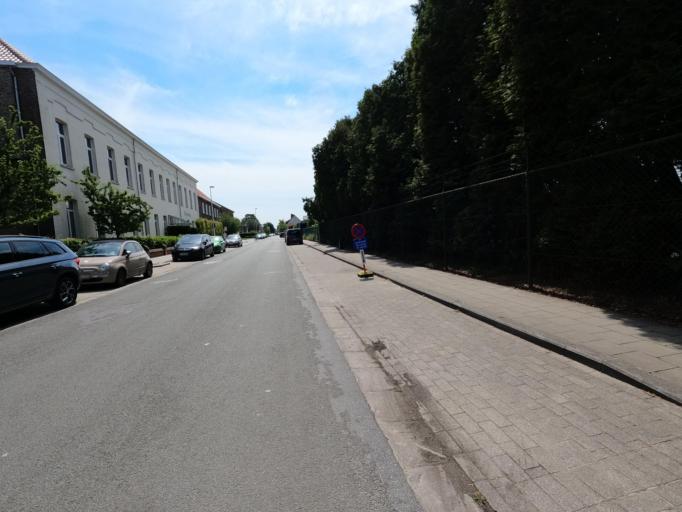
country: BE
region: Flanders
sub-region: Provincie Antwerpen
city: Essen
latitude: 51.4697
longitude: 4.4607
